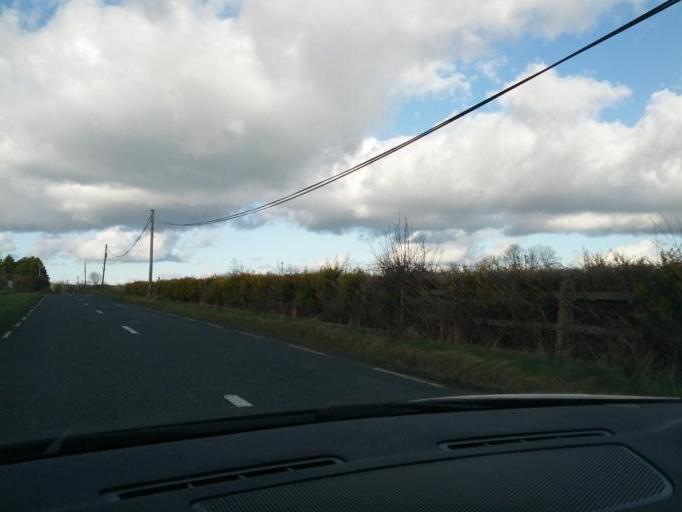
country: IE
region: Connaught
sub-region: Roscommon
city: Castlerea
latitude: 53.6480
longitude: -8.5216
